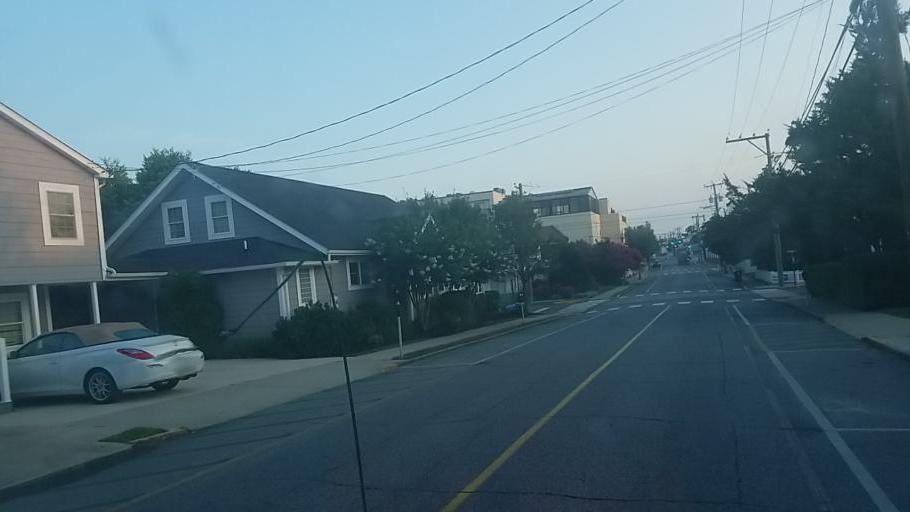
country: US
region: Delaware
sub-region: Sussex County
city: Rehoboth Beach
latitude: 38.7143
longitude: -75.0786
